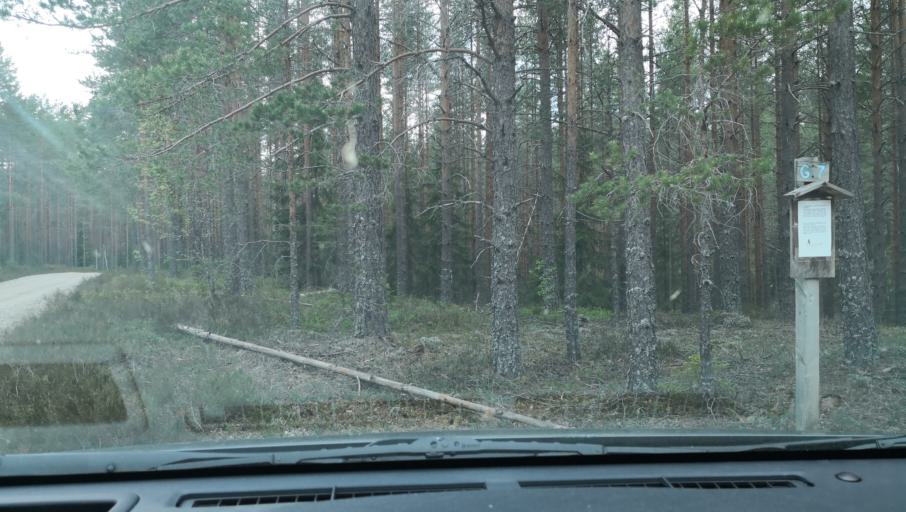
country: SE
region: Vaestmanland
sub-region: Skinnskattebergs Kommun
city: Skinnskatteberg
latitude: 59.8022
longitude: 15.4971
